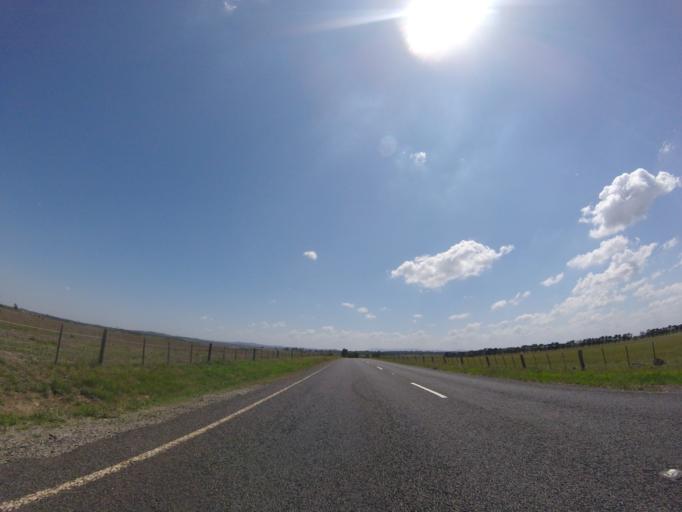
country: AU
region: Victoria
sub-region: Hume
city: Greenvale
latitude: -37.6160
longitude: 144.8149
